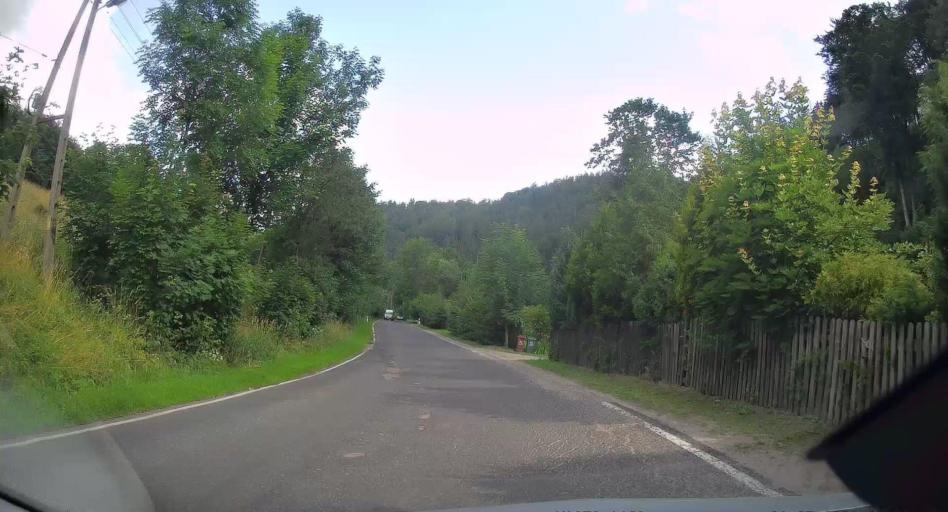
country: PL
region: Lower Silesian Voivodeship
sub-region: Powiat walbrzyski
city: Walim
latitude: 50.7114
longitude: 16.4347
